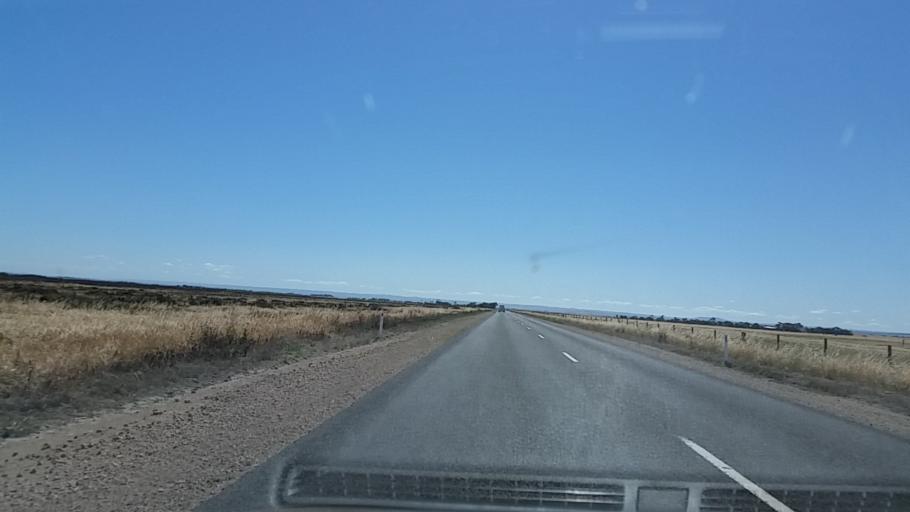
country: AU
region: South Australia
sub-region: Murray Bridge
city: Murray Bridge
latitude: -35.3157
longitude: 139.2389
